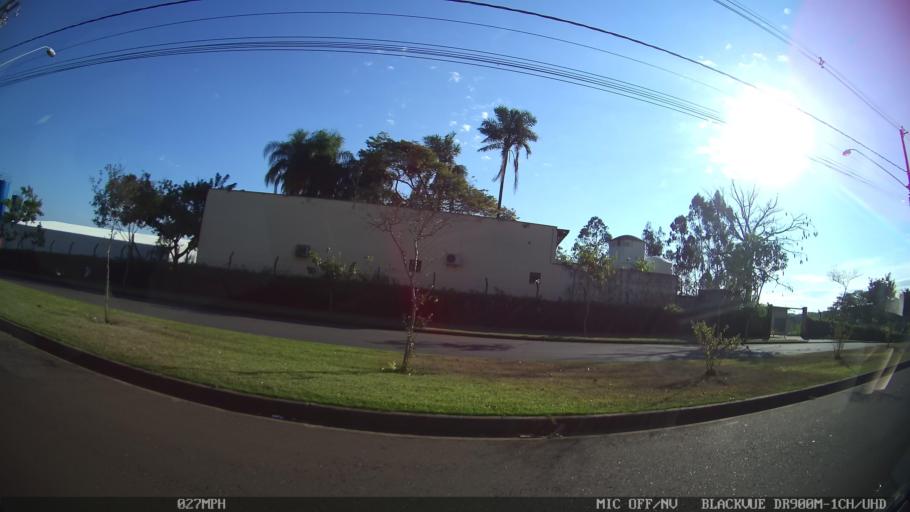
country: BR
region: Sao Paulo
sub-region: Piracicaba
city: Piracicaba
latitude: -22.6932
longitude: -47.6240
